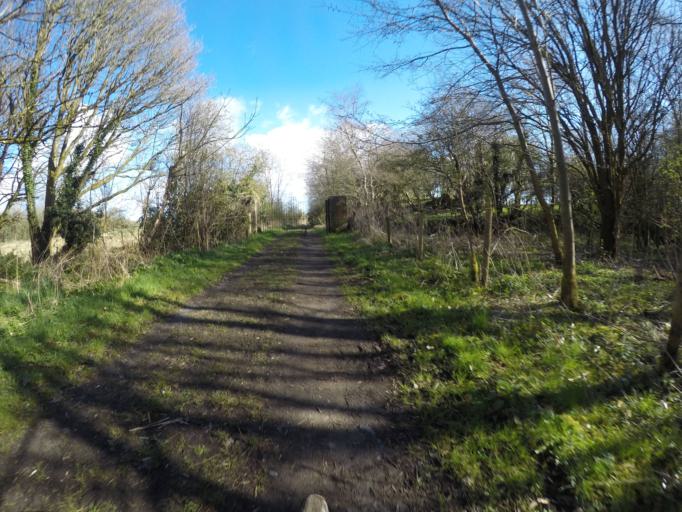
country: GB
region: Scotland
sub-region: North Ayrshire
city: Irvine
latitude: 55.6487
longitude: -4.6593
